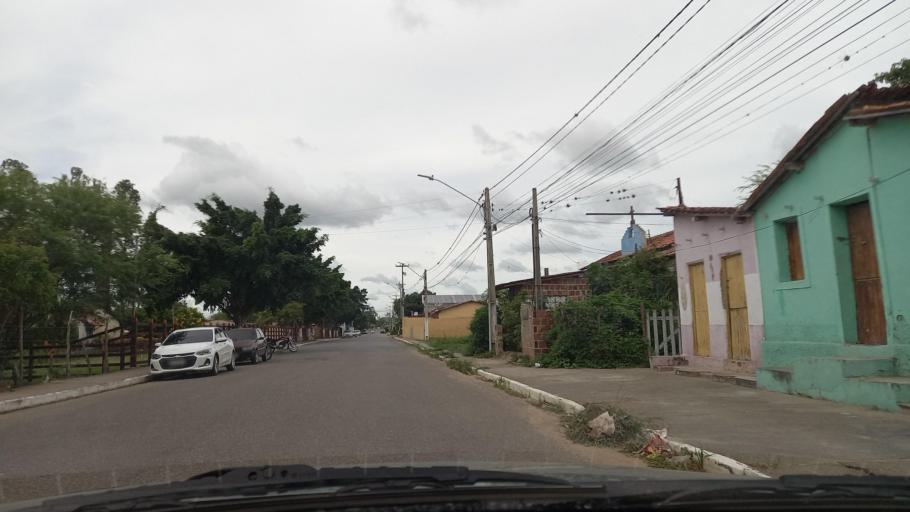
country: BR
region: Pernambuco
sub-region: Gravata
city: Gravata
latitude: -8.2077
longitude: -35.5889
